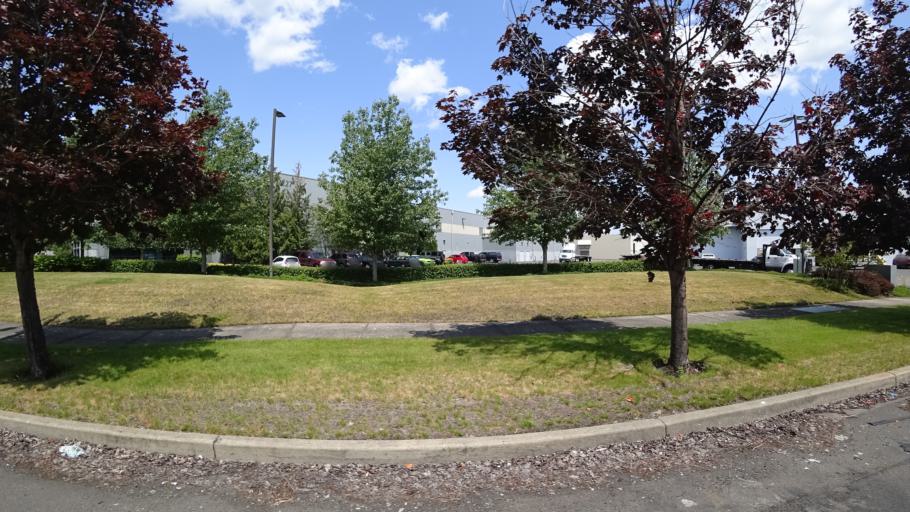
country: US
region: Washington
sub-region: Clark County
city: Lake Shore
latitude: 45.6291
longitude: -122.7492
